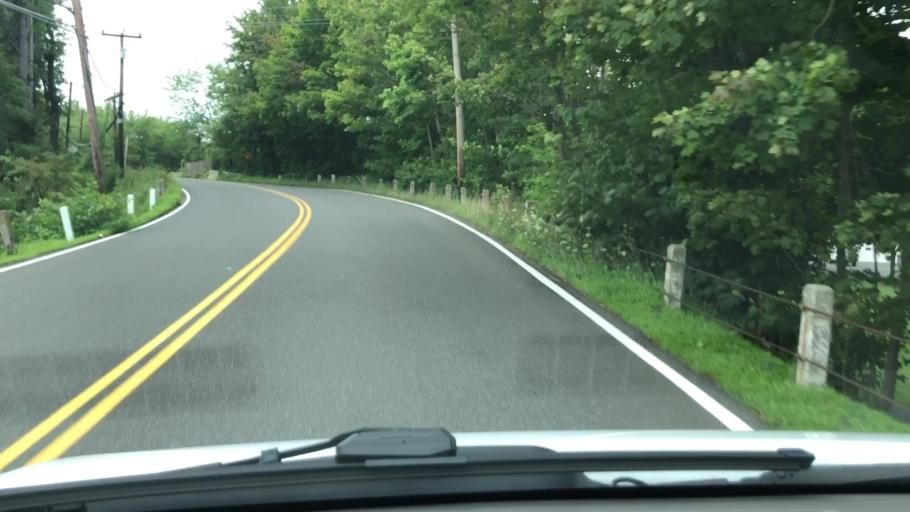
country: US
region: Massachusetts
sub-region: Franklin County
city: South Deerfield
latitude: 42.4946
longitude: -72.6075
